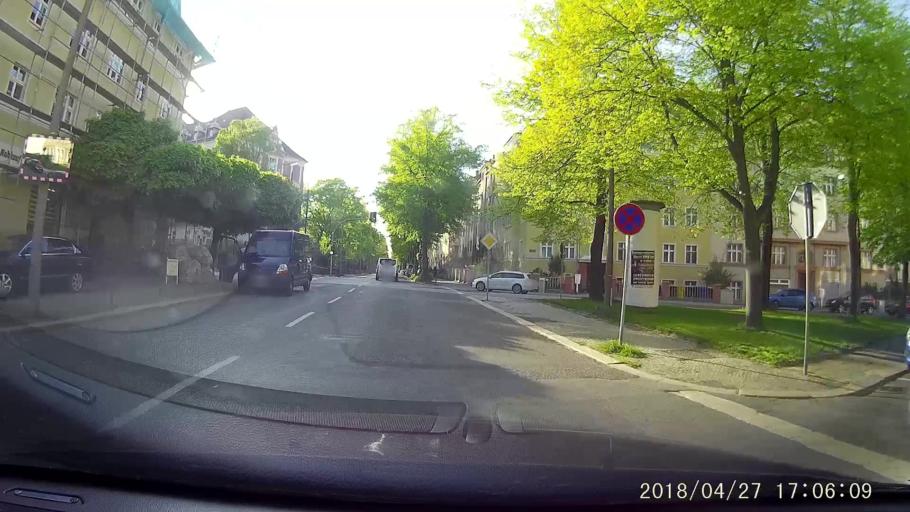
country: DE
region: Saxony
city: Goerlitz
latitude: 51.1443
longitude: 14.9678
